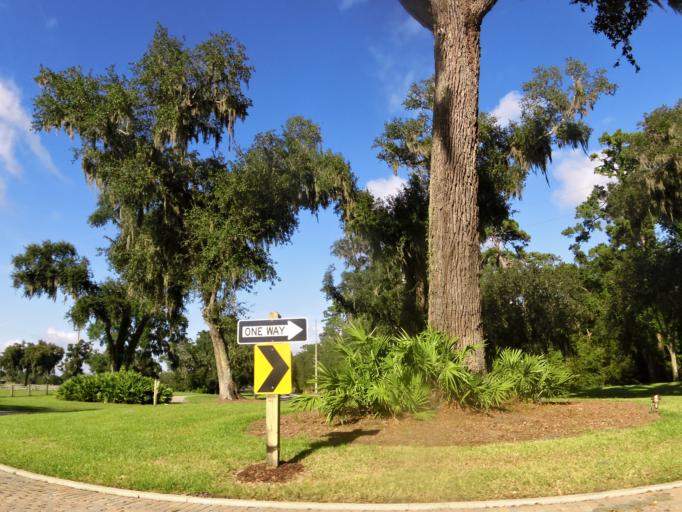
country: US
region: Georgia
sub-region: Glynn County
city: Saint Simon Mills
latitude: 31.2165
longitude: -81.3758
